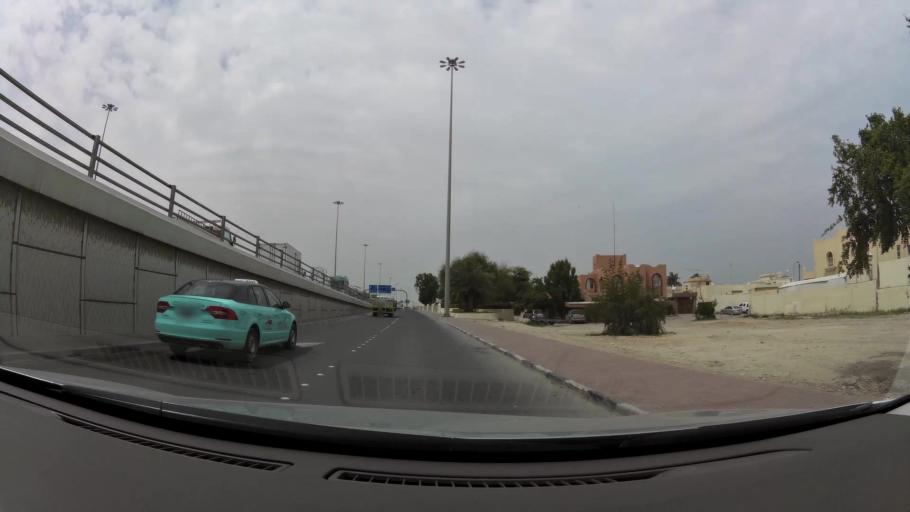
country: QA
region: Baladiyat ar Rayyan
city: Ar Rayyan
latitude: 25.3233
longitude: 51.4690
